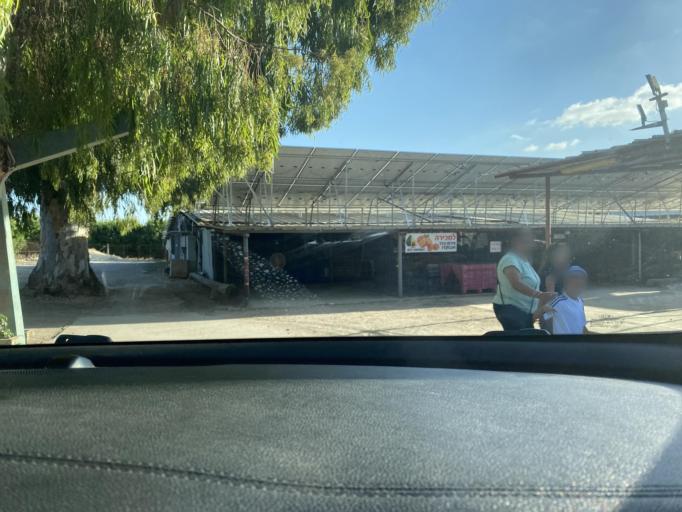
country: IL
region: Northern District
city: Shelomi
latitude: 33.0681
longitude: 35.1380
